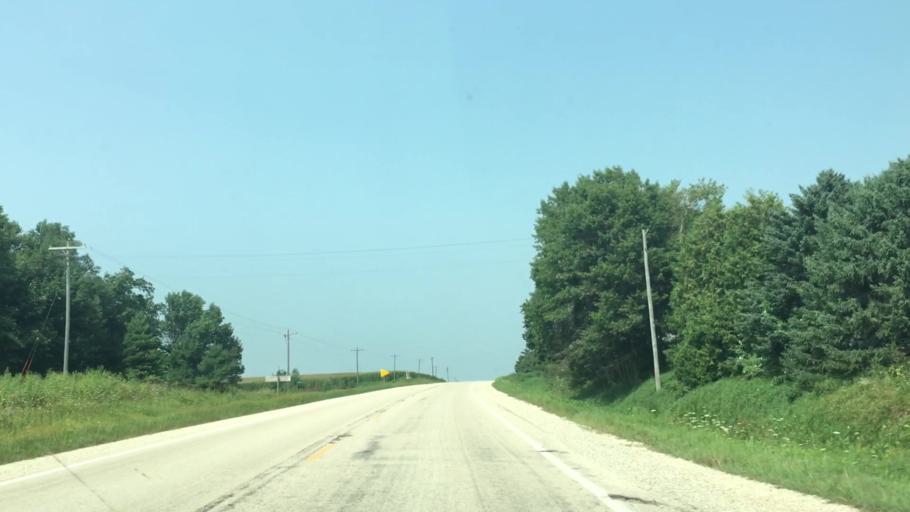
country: US
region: Iowa
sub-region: Fayette County
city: West Union
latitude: 43.0043
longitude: -91.8245
